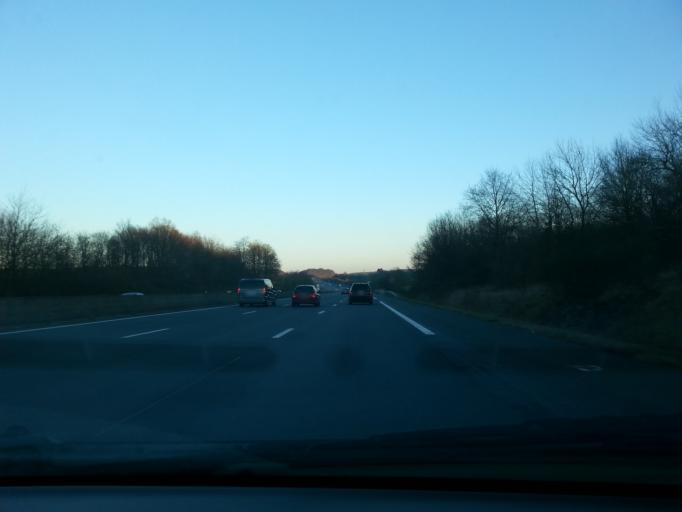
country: FR
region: Centre
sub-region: Departement d'Eure-et-Loir
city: Authon-du-Perche
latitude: 48.1926
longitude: 0.8248
